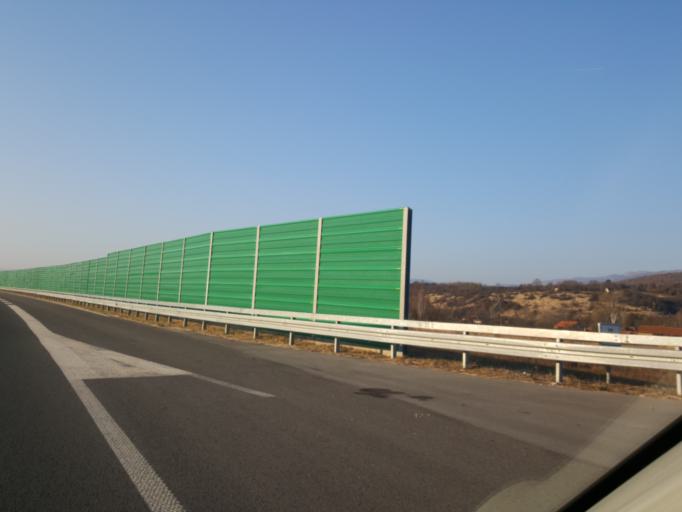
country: RS
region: Central Serbia
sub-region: Pirotski Okrug
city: Dimitrovgrad
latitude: 43.0569
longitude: 22.6946
